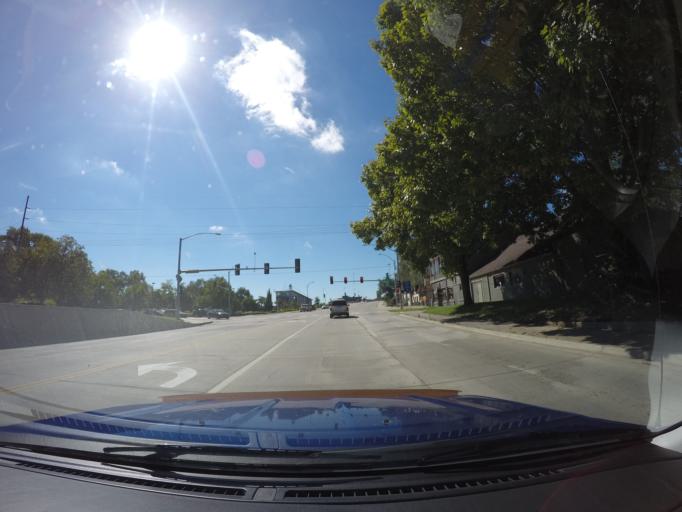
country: US
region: Kansas
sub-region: Douglas County
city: Lawrence
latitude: 38.9783
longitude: -95.2353
